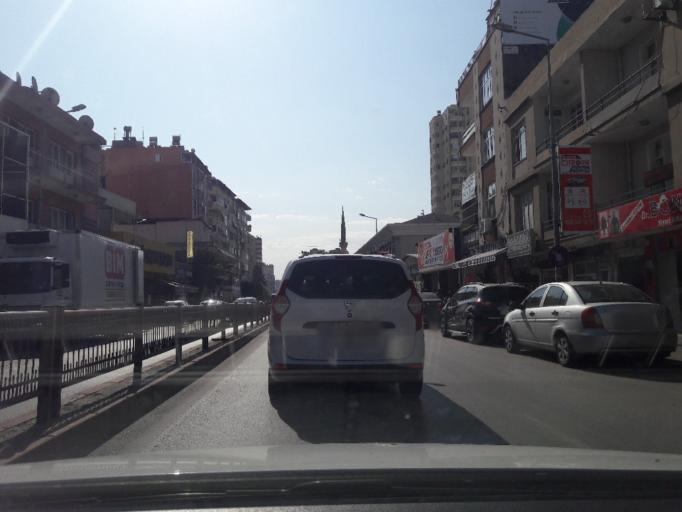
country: TR
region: Adana
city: Adana
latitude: 37.0137
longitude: 35.3225
